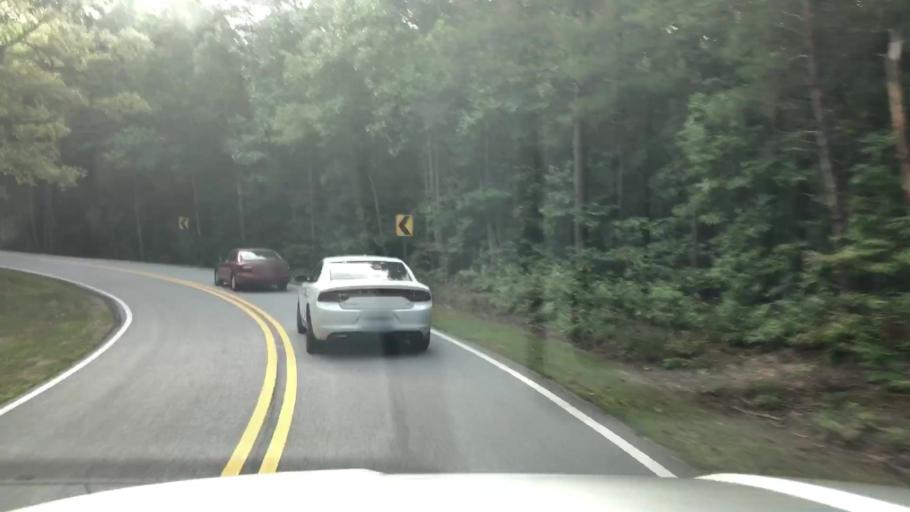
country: US
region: Georgia
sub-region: Bartow County
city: Euharlee
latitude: 34.0471
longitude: -84.8619
